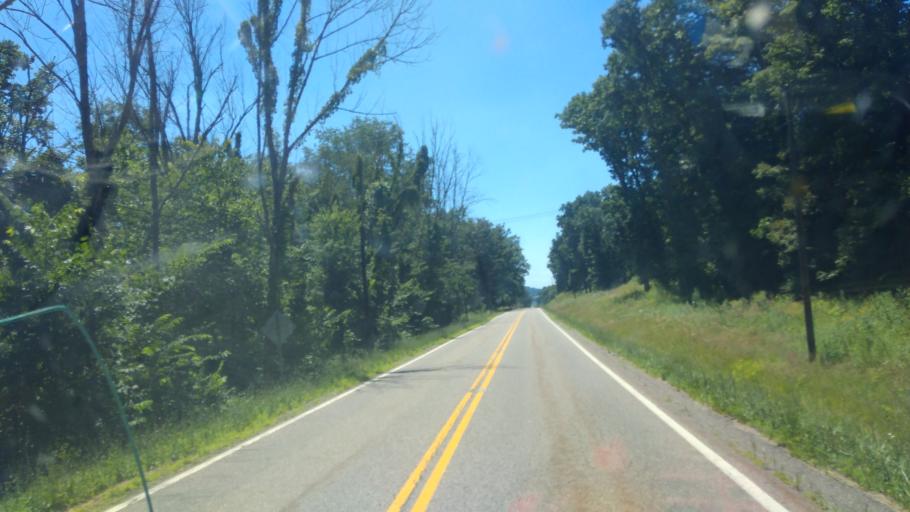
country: US
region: Ohio
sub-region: Carroll County
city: Carrollton
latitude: 40.6137
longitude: -80.9775
